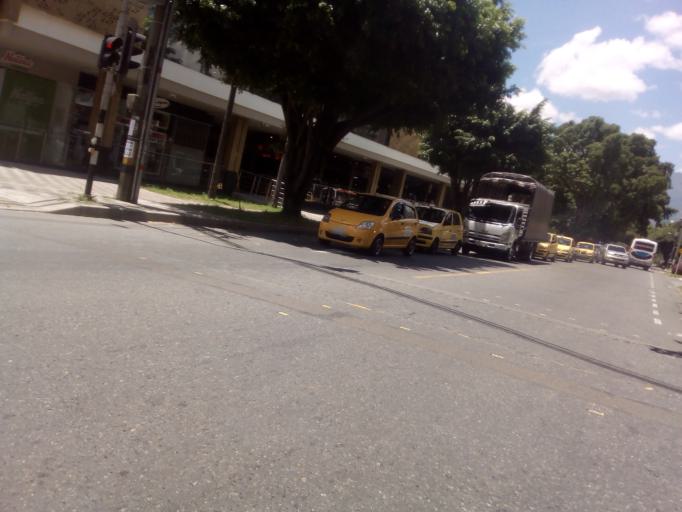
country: CO
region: Antioquia
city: Medellin
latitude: 6.2623
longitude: -75.5878
